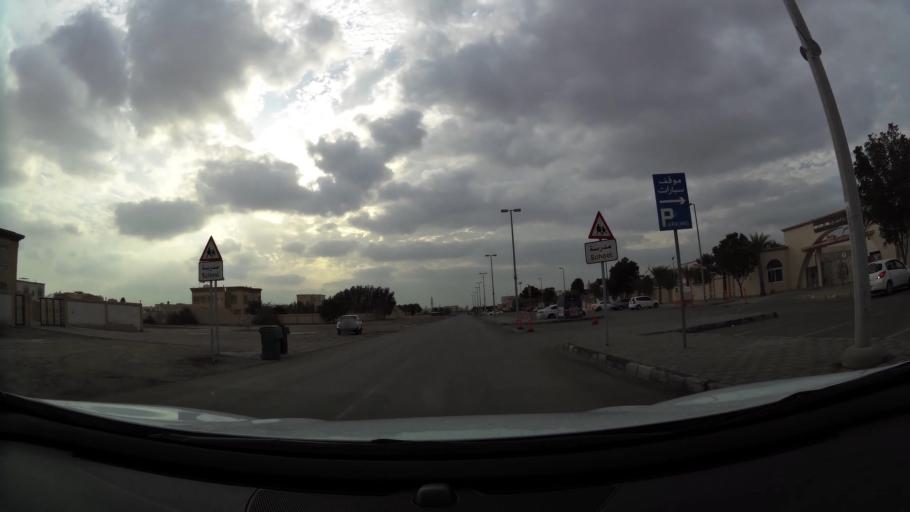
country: AE
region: Abu Dhabi
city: Abu Dhabi
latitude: 24.3604
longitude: 54.5513
